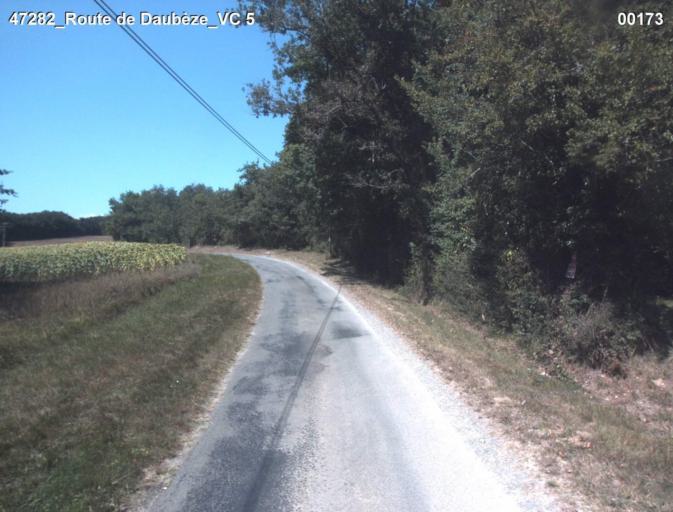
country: FR
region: Aquitaine
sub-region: Departement du Lot-et-Garonne
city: Laplume
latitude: 44.0851
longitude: 0.5334
